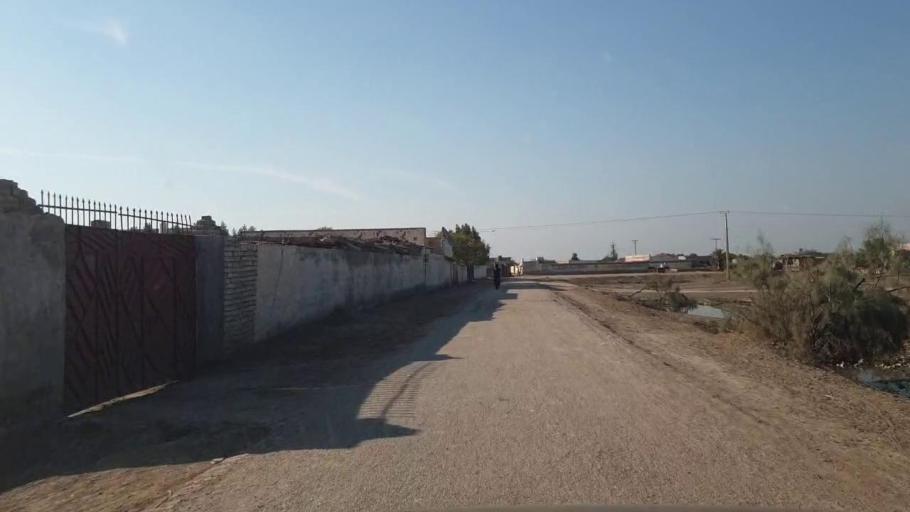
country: PK
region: Sindh
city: Shahpur Chakar
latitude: 26.1792
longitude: 68.6638
